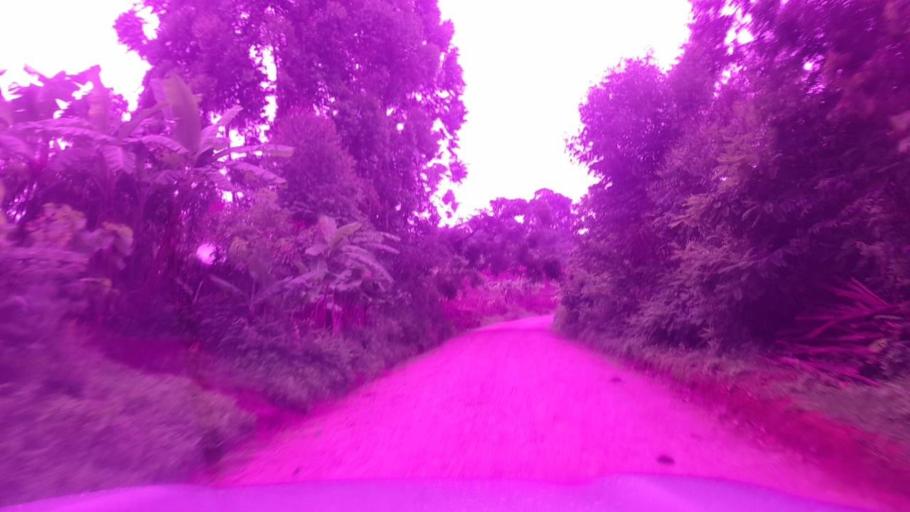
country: ET
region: Southern Nations, Nationalities, and People's Region
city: Bonga
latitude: 7.4669
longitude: 36.1236
